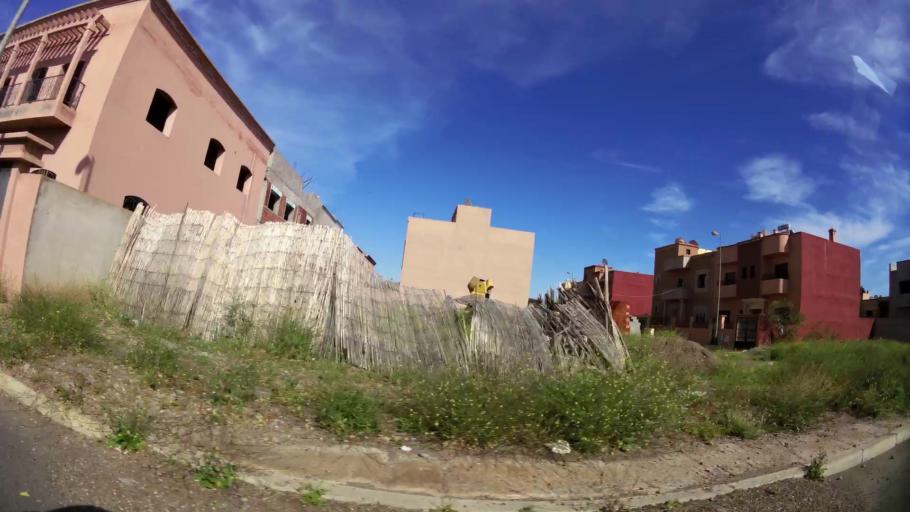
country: MA
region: Marrakech-Tensift-Al Haouz
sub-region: Marrakech
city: Marrakesh
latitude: 31.6474
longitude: -8.0414
